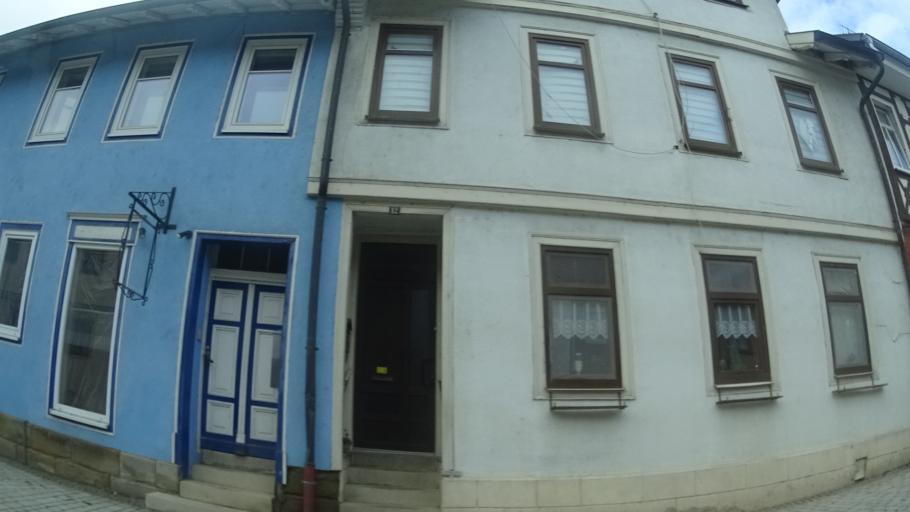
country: DE
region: Thuringia
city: Romhild
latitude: 50.3960
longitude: 10.5375
